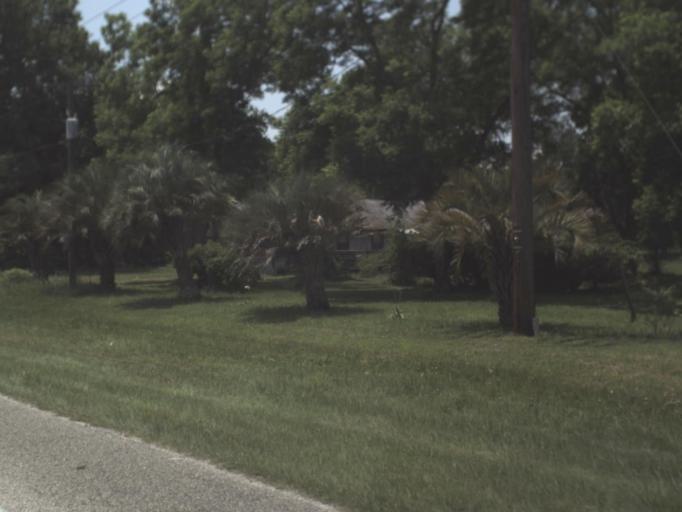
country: US
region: Florida
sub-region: Bradford County
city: Starke
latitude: 29.9924
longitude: -82.0947
